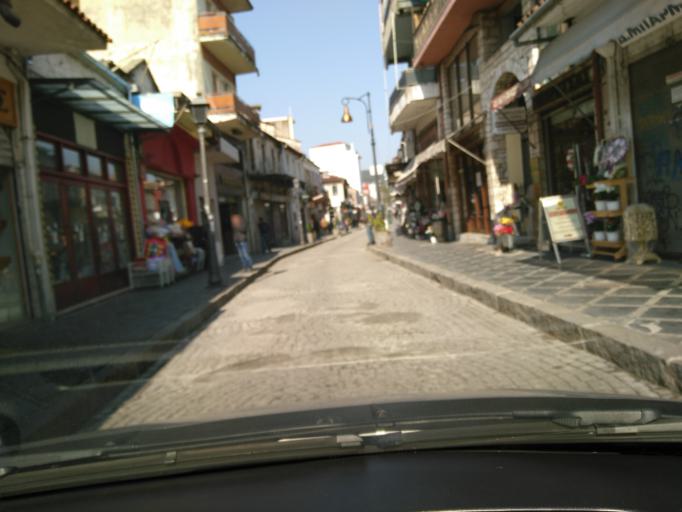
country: GR
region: Epirus
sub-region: Nomos Ioanninon
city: Ioannina
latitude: 39.6692
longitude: 20.8553
